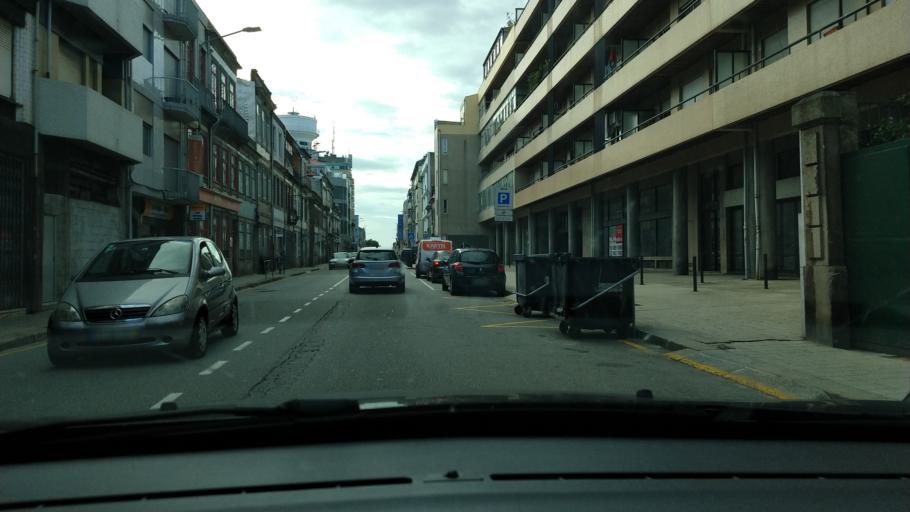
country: PT
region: Porto
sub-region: Porto
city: Porto
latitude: 41.1587
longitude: -8.6013
